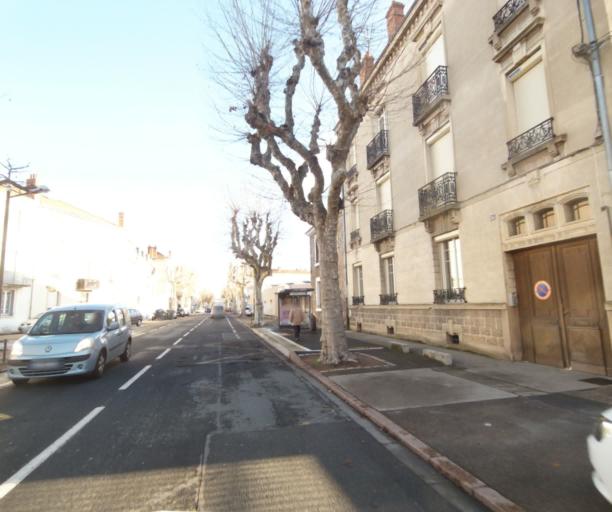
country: FR
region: Rhone-Alpes
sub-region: Departement de la Loire
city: Roanne
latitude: 46.0428
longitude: 4.0668
